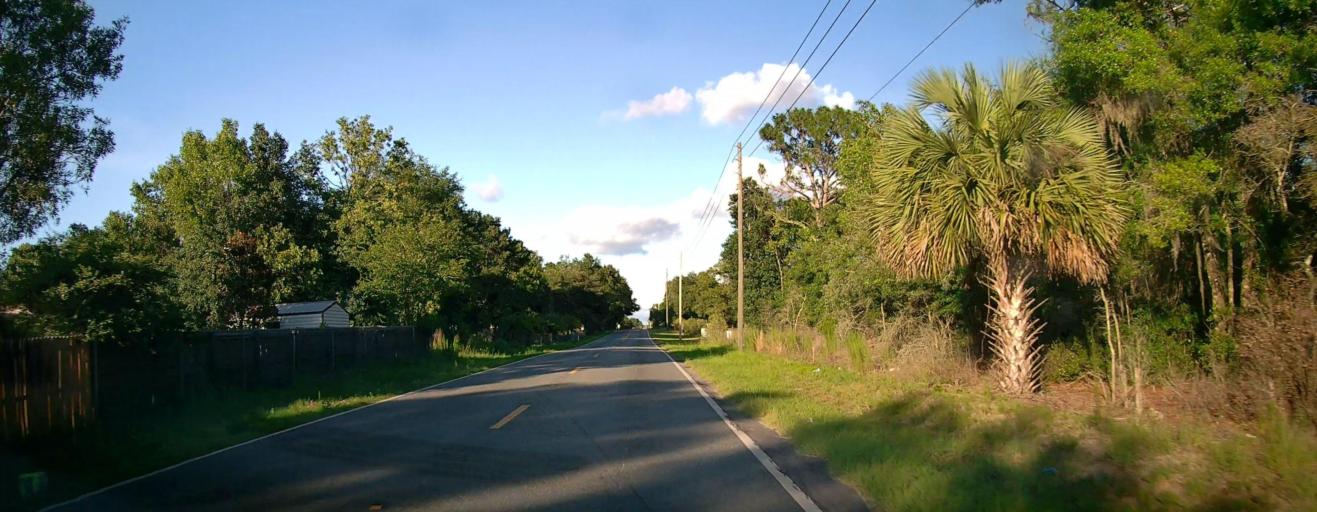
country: US
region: Florida
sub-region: Marion County
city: Silver Springs Shores
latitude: 29.0654
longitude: -82.0111
